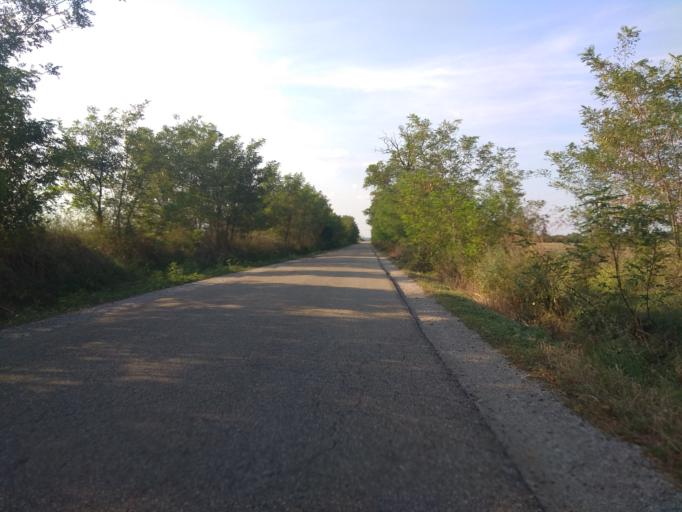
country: HU
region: Borsod-Abauj-Zemplen
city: Harsany
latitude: 47.9121
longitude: 20.7419
